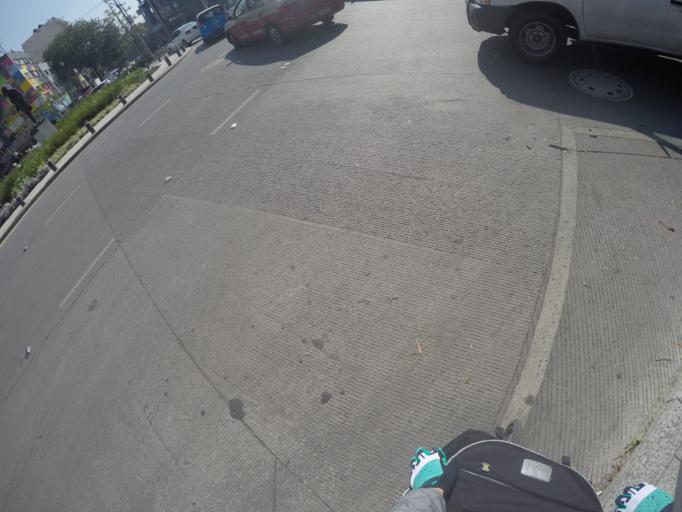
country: MX
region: Mexico
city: Naucalpan de Juarez
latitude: 19.4548
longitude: -99.2224
